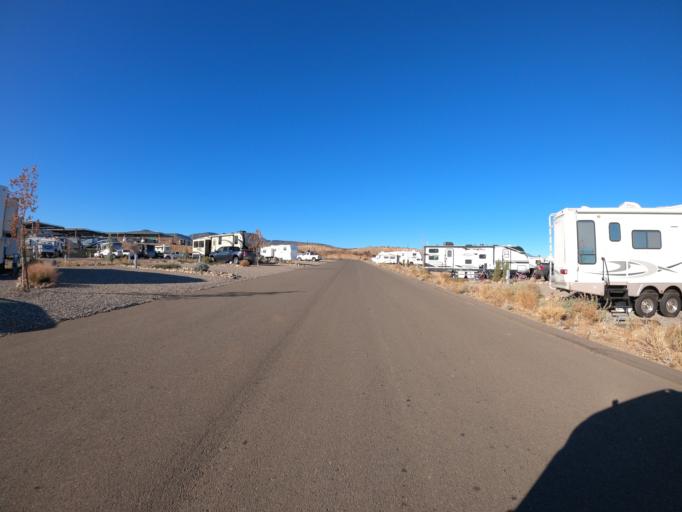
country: US
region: Arizona
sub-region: Yavapai County
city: Camp Verde
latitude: 34.5859
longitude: -111.8837
